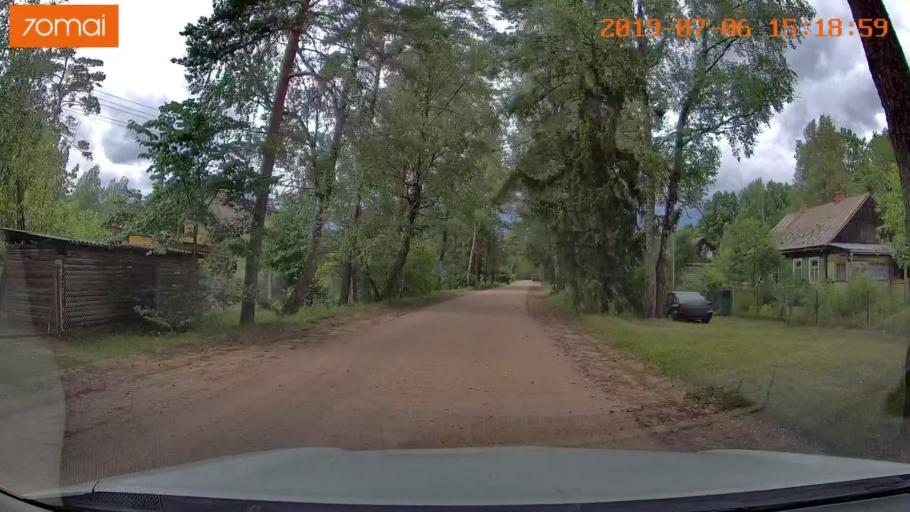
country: BY
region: Minsk
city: Ivyanyets
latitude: 53.9943
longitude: 26.6488
